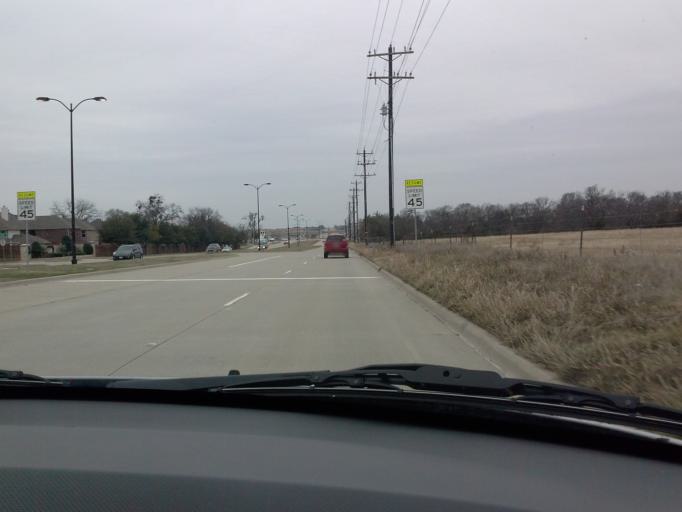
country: US
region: Texas
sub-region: Collin County
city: Frisco
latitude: 33.1259
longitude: -96.7508
